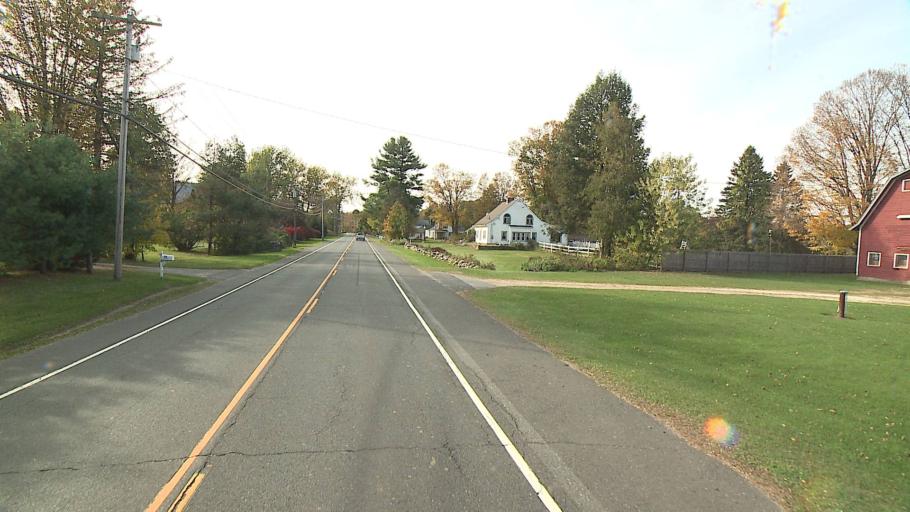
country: US
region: Connecticut
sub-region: Litchfield County
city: Canaan
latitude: 42.0113
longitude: -73.2659
